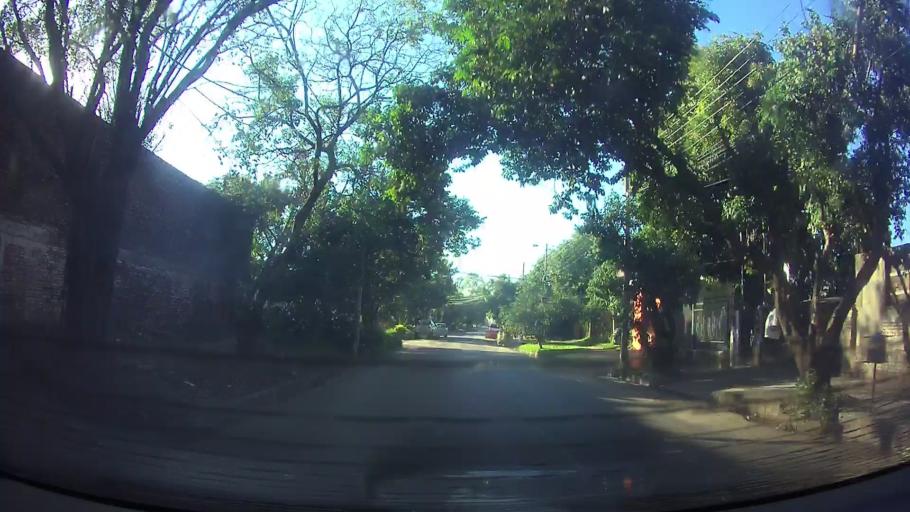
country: PY
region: Central
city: Fernando de la Mora
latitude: -25.2647
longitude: -57.5502
